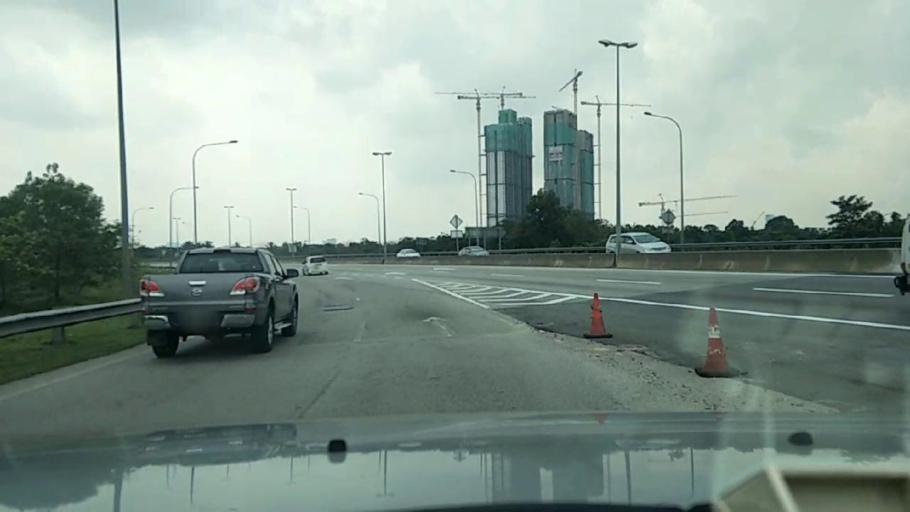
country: MY
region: Putrajaya
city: Putrajaya
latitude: 2.9301
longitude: 101.6244
